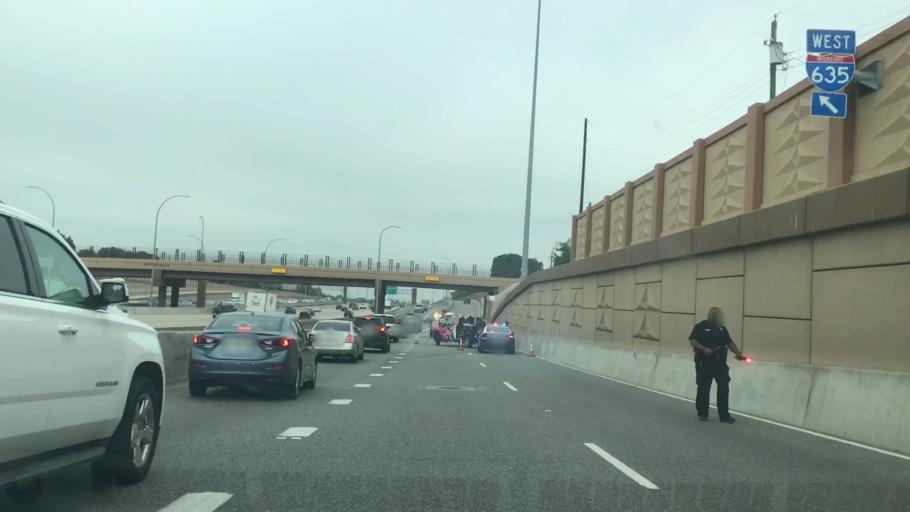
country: US
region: Texas
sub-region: Dallas County
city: Addison
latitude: 32.9223
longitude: -96.8469
